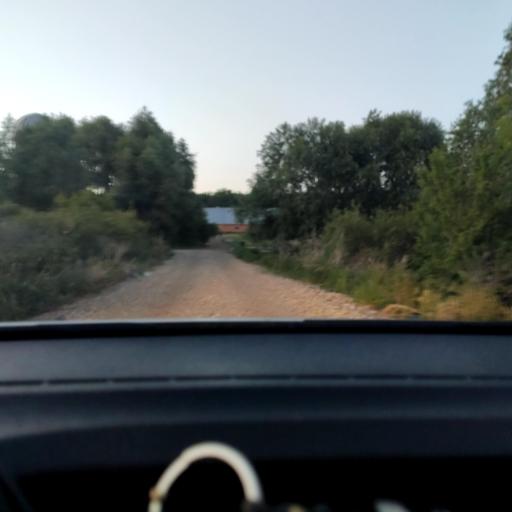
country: RU
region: Bashkortostan
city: Mikhaylovka
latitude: 54.8164
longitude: 55.8043
